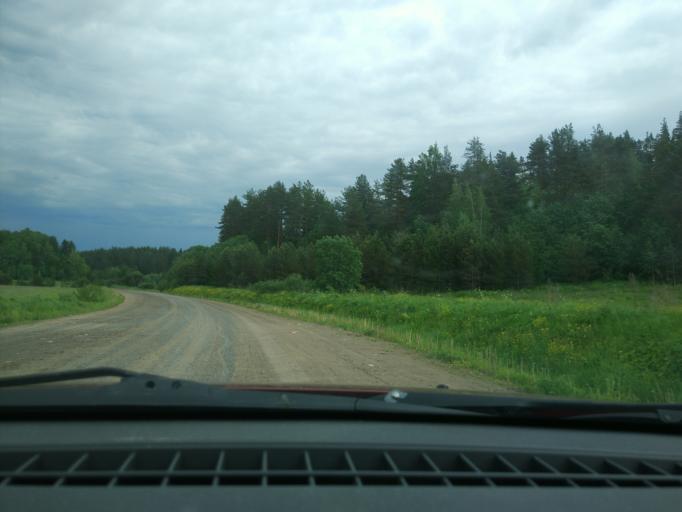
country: RU
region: Leningrad
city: Kuznechnoye
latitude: 61.2802
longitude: 29.8524
